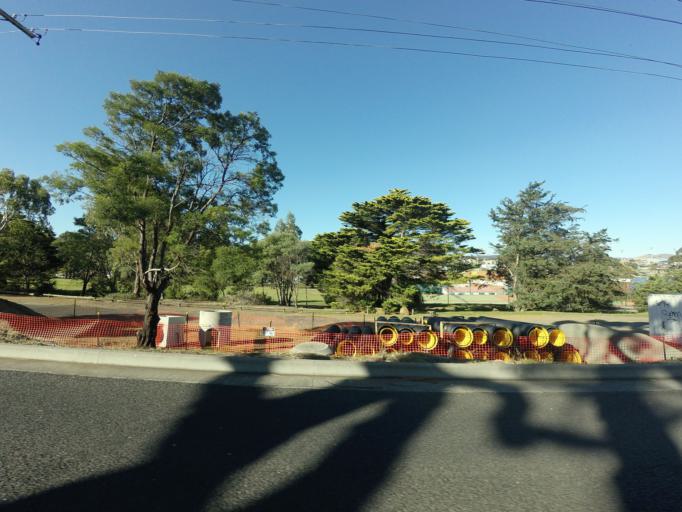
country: AU
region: Tasmania
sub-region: Clarence
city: Bellerive
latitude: -42.8685
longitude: 147.3633
